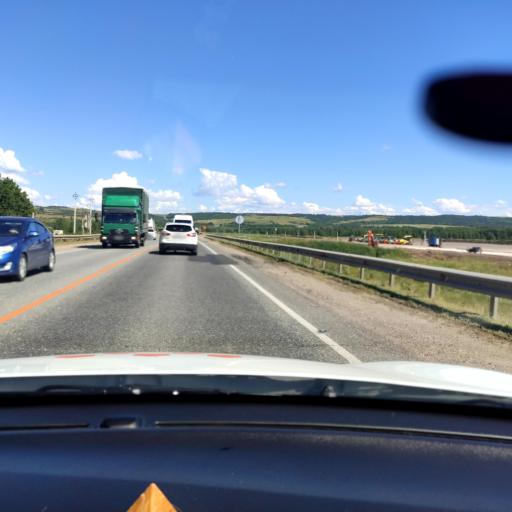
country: RU
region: Tatarstan
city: Sviyazhsk
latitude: 55.7100
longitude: 48.6825
